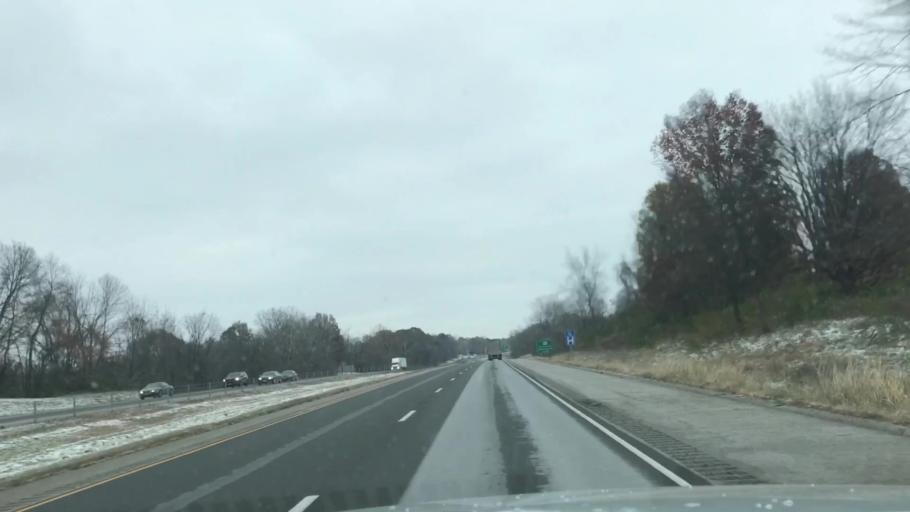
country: US
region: Illinois
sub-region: Madison County
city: Glen Carbon
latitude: 38.7569
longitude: -89.9714
